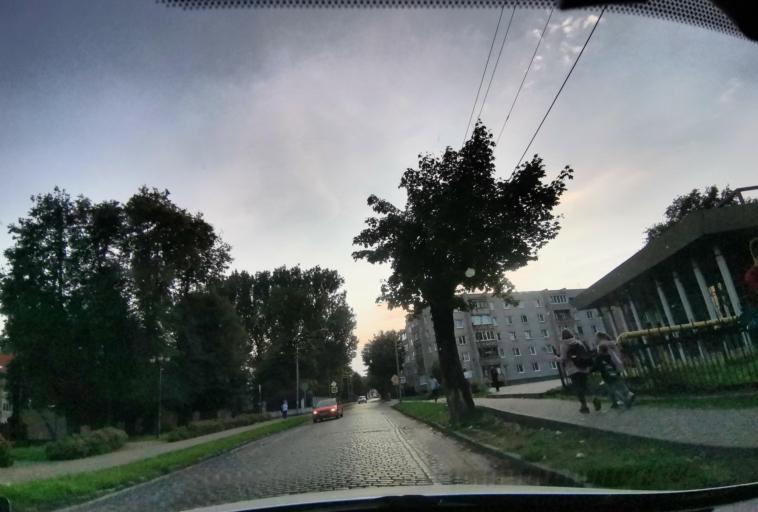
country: RU
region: Kaliningrad
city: Sovetsk
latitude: 55.0786
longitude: 21.8925
